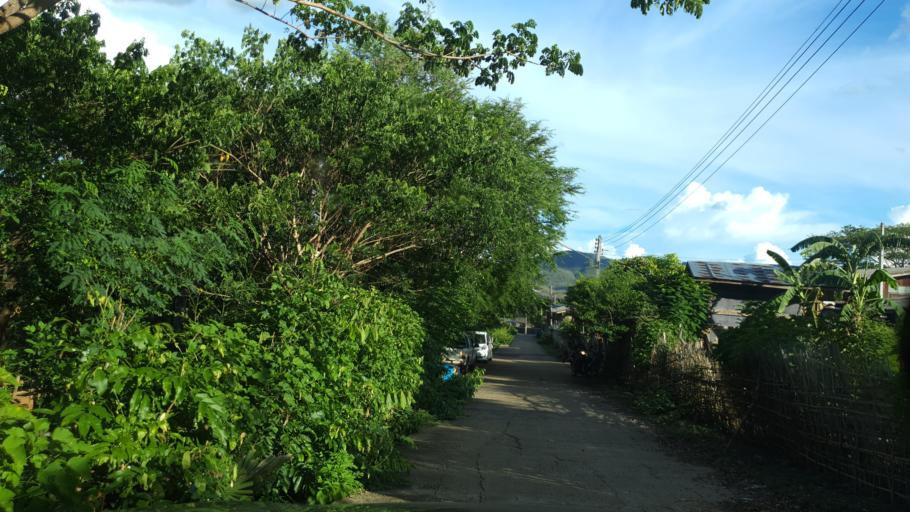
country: TH
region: Lampang
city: Sop Prap
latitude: 17.8774
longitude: 99.2980
